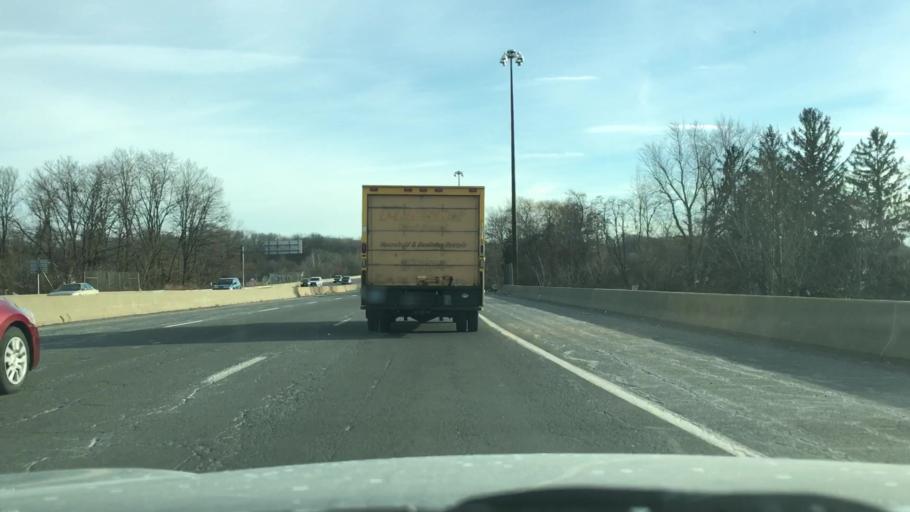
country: US
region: Massachusetts
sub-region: Hampden County
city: North Chicopee
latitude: 42.1892
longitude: -72.6095
